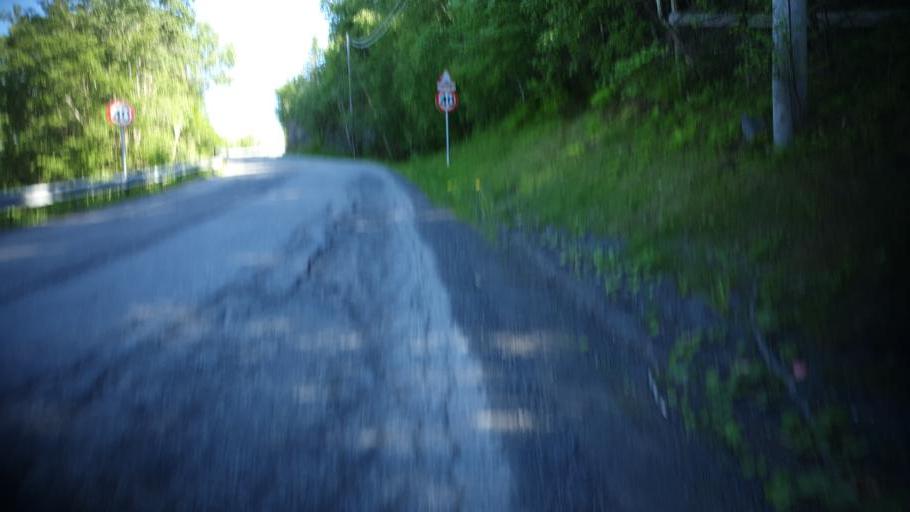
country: NO
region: Sor-Trondelag
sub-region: Malvik
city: Malvik
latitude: 63.4320
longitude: 10.6003
